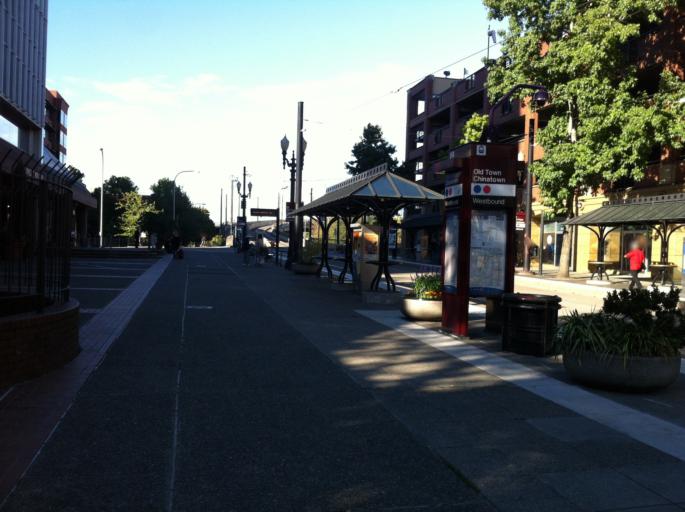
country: US
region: Oregon
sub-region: Multnomah County
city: Portland
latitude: 45.5246
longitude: -122.6717
